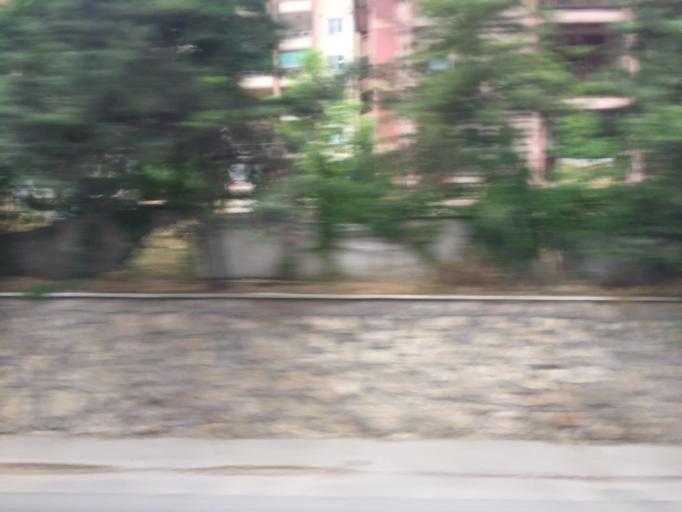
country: TR
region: Gaziantep
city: Gaziantep
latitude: 37.0516
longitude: 37.4210
